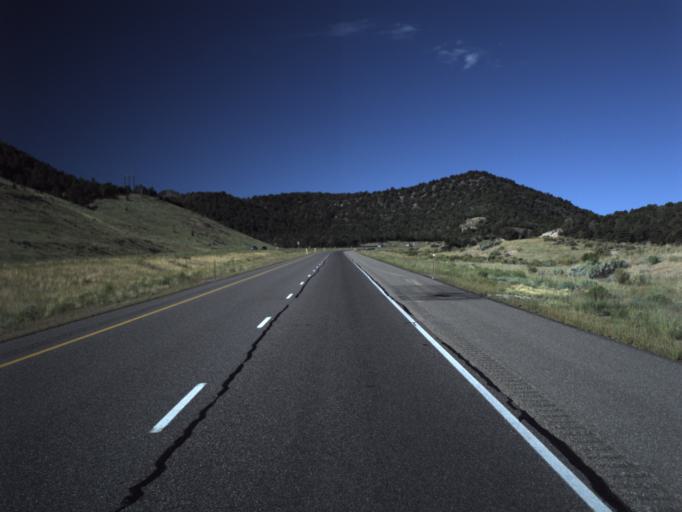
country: US
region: Utah
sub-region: Sevier County
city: Monroe
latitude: 38.5508
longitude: -112.3684
